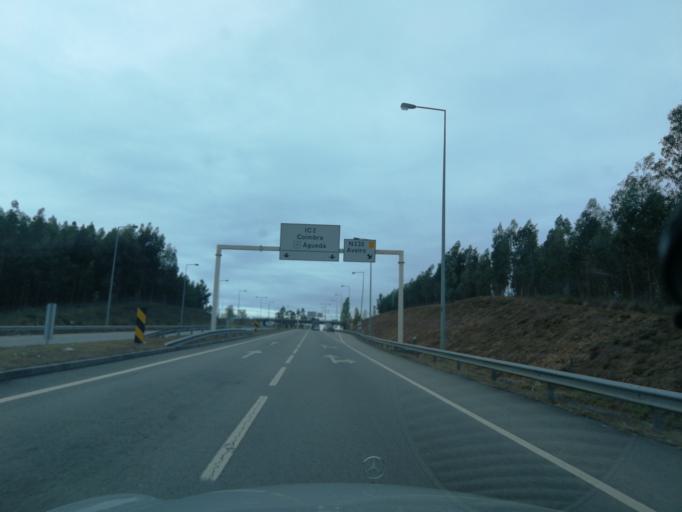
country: PT
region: Aveiro
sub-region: Agueda
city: Valongo
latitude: 40.5986
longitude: -8.4683
